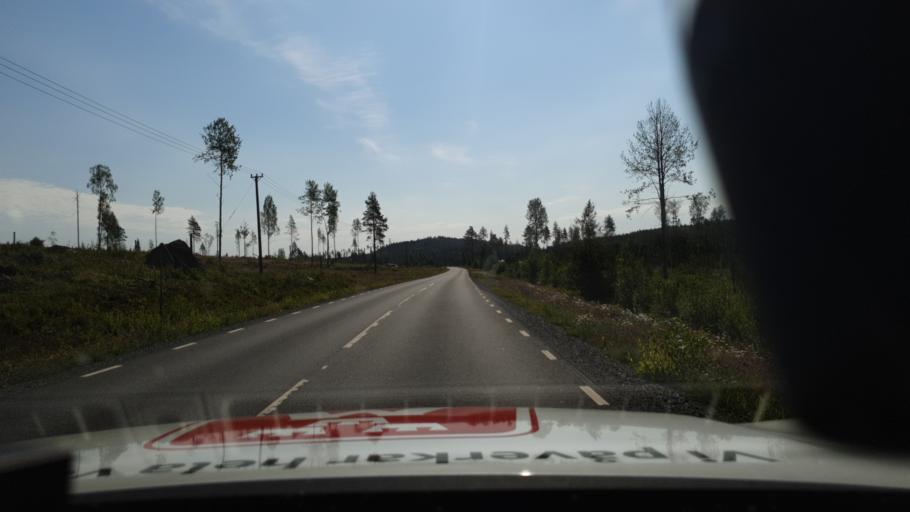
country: SE
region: Norrbotten
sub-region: Bodens Kommun
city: Saevast
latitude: 65.8356
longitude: 21.8579
